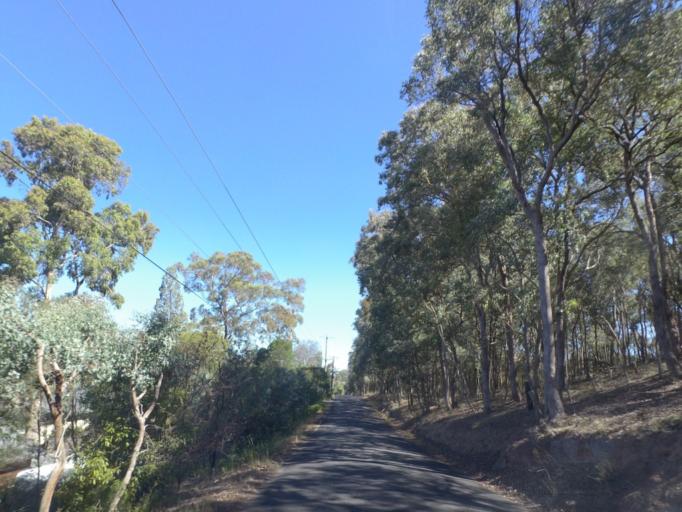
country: AU
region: Victoria
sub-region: Yarra Ranges
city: Chirnside Park
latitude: -37.7211
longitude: 145.2855
